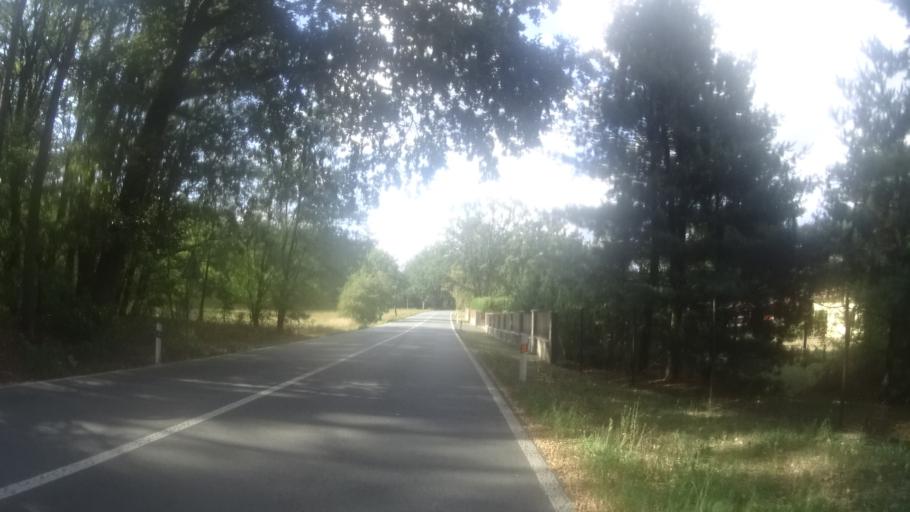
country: CZ
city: Albrechtice nad Orlici
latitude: 50.1269
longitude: 16.0655
